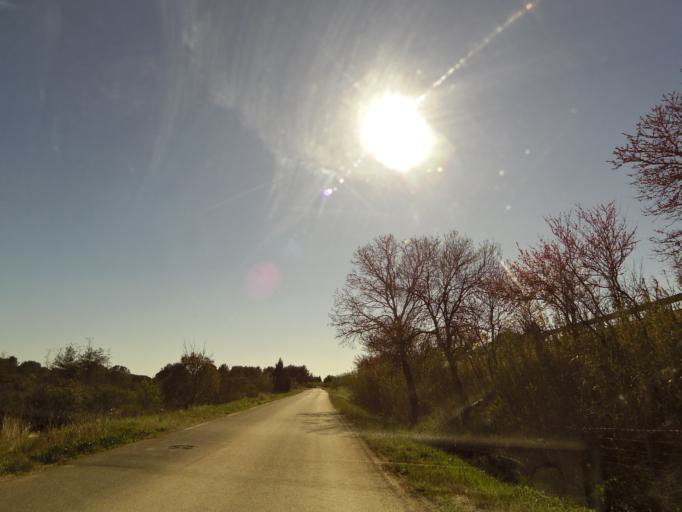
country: FR
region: Languedoc-Roussillon
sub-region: Departement de l'Herault
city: Villetelle
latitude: 43.7186
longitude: 4.1412
